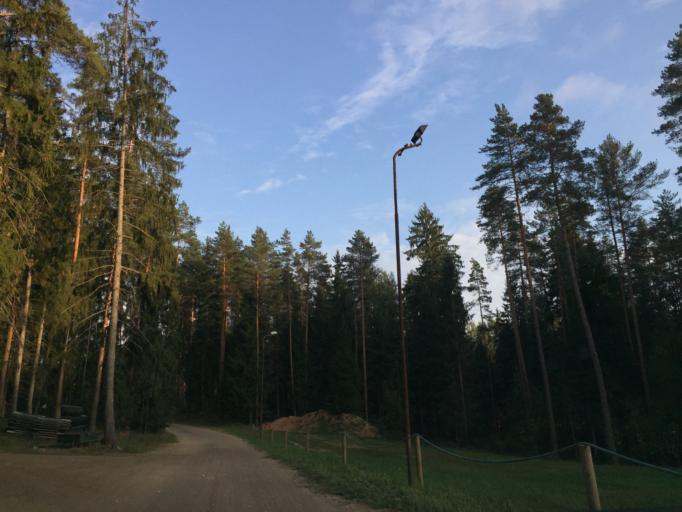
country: LV
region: Baldone
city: Baldone
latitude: 56.7698
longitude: 24.4006
